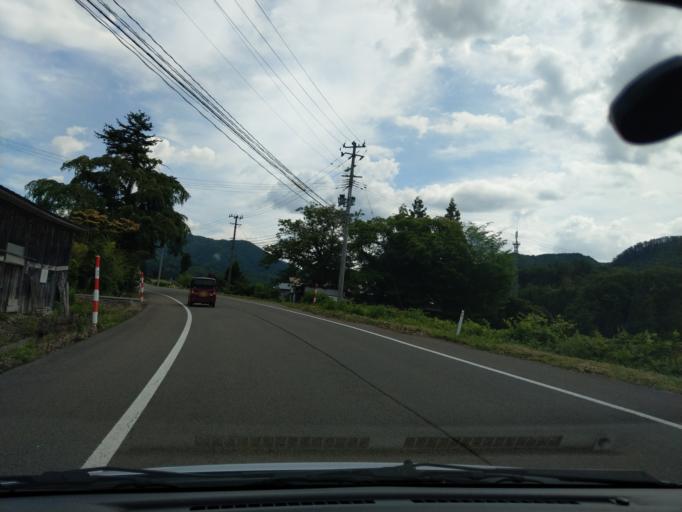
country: JP
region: Akita
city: Kakunodatemachi
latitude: 39.6983
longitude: 140.5798
